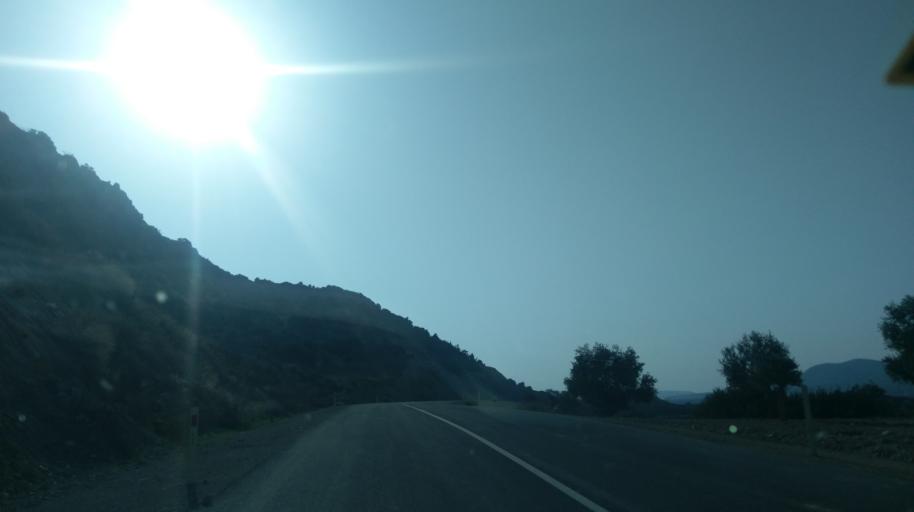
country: CY
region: Ammochostos
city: Rizokarpaso
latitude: 35.5236
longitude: 34.2956
